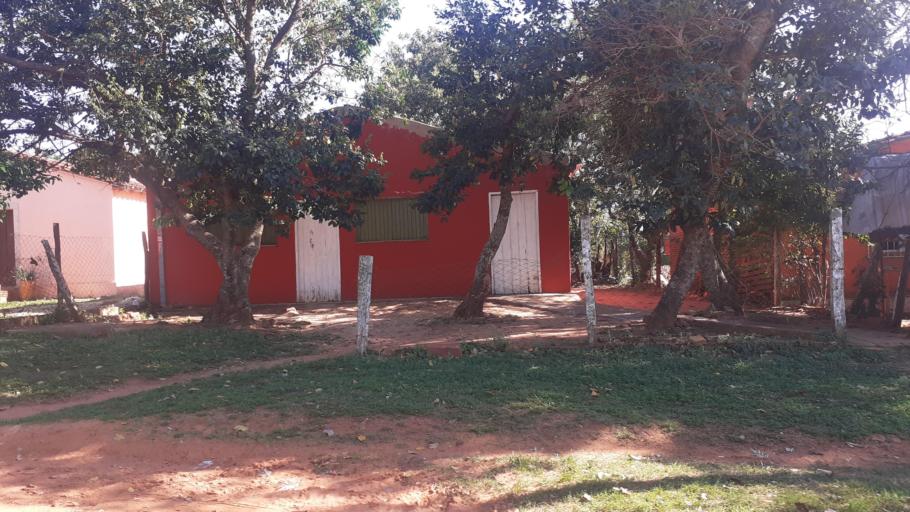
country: PY
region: Misiones
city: San Juan Bautista
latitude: -26.6650
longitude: -57.1246
